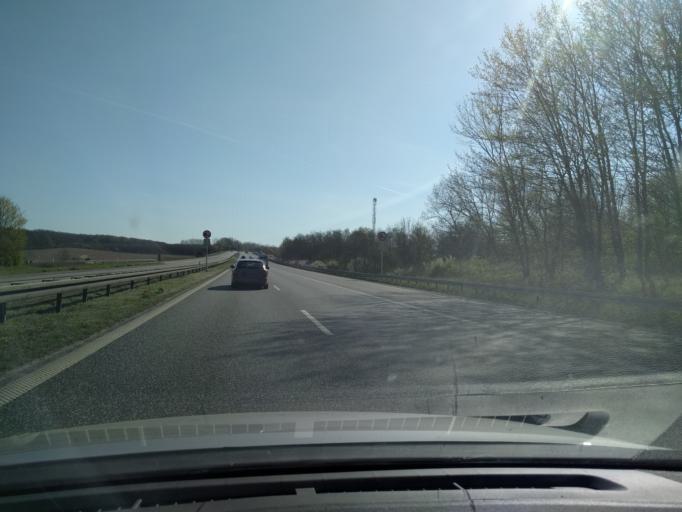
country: DK
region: Zealand
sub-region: Slagelse Kommune
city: Slagelse
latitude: 55.4187
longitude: 11.4178
